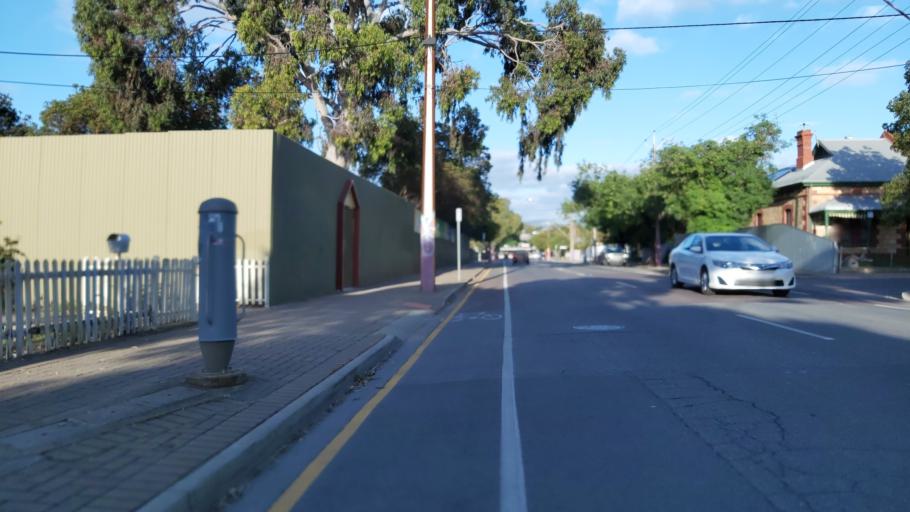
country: AU
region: South Australia
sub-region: Unley
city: Wayville
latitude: -34.9487
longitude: 138.5866
